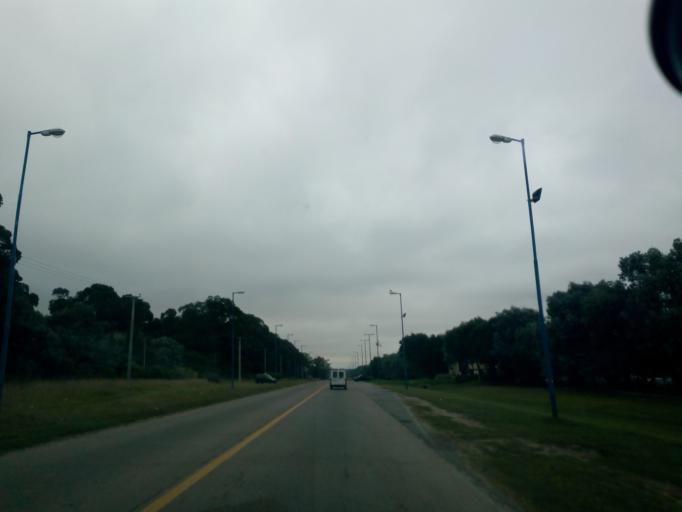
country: AR
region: Buenos Aires
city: Mar del Plata
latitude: -38.0751
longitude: -57.5787
